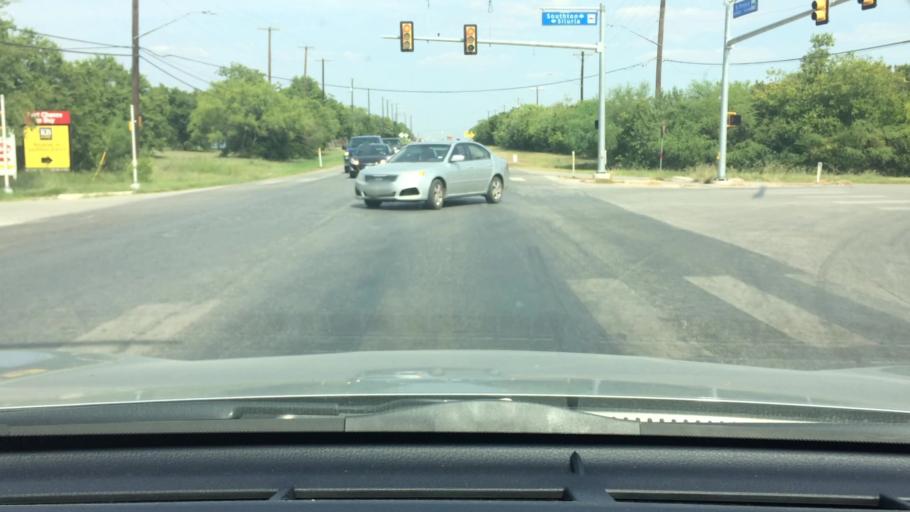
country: US
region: Texas
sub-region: Bexar County
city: China Grove
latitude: 29.3266
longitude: -98.4332
